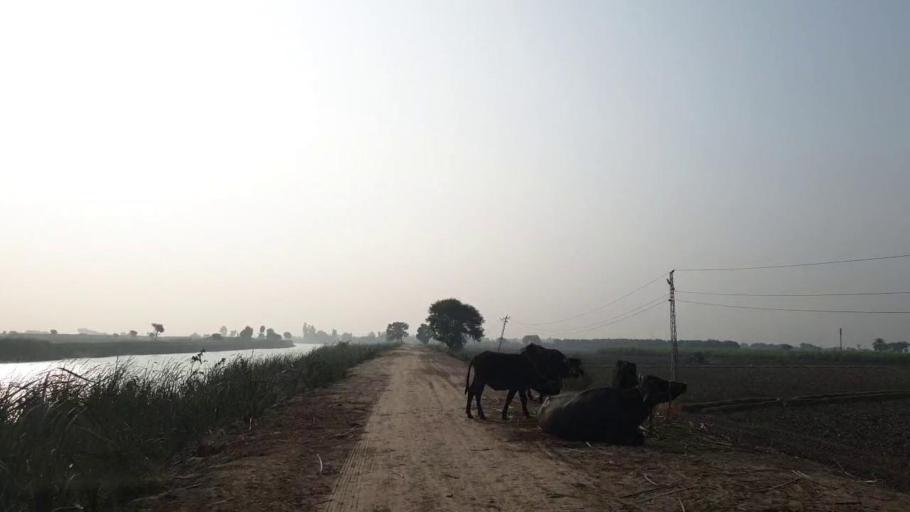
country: PK
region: Sindh
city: Tando Muhammad Khan
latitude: 25.0975
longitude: 68.5762
